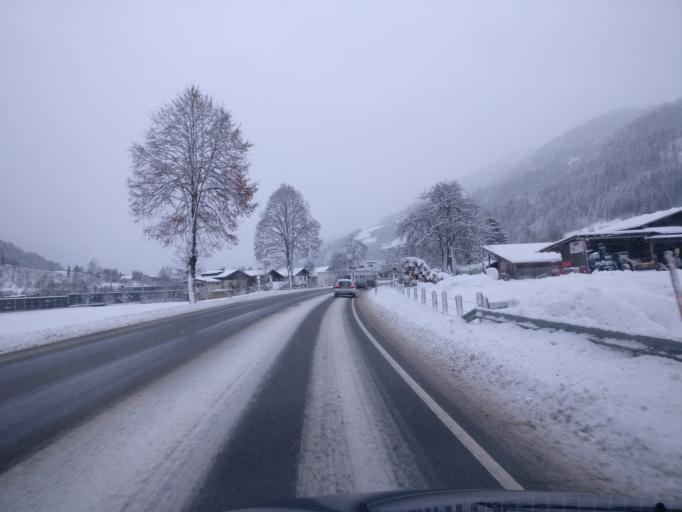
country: AT
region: Salzburg
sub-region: Politischer Bezirk Sankt Johann im Pongau
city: Bischofshofen
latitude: 47.3974
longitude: 13.2239
